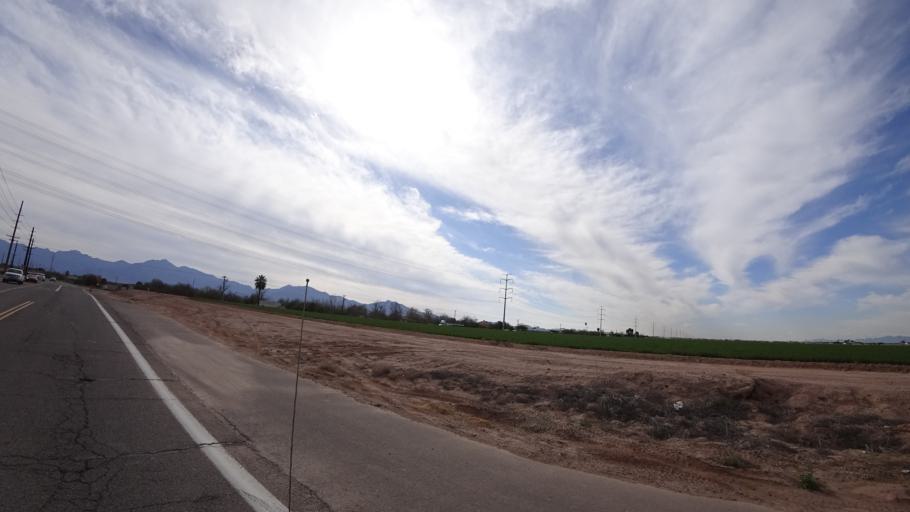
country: US
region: Arizona
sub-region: Maricopa County
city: Tolleson
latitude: 33.4076
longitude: -112.2551
